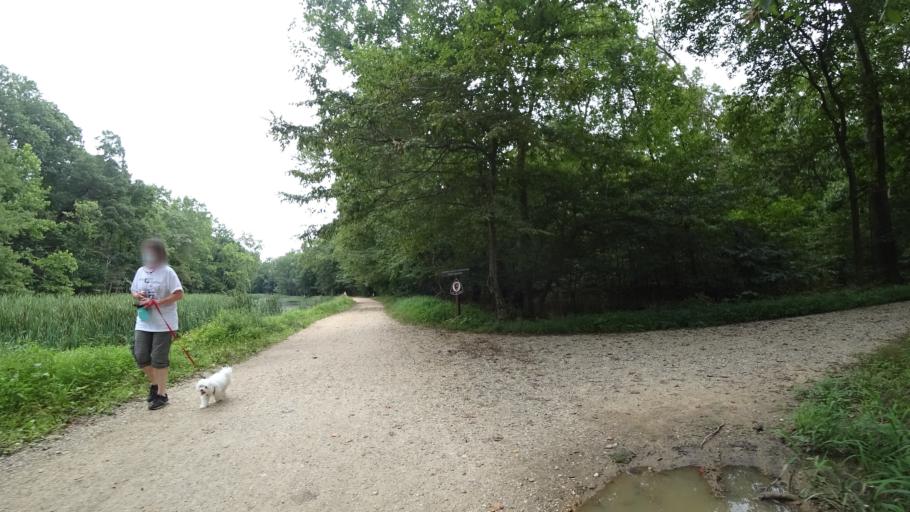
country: US
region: Maryland
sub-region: Montgomery County
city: Potomac
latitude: 38.9774
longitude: -77.2152
